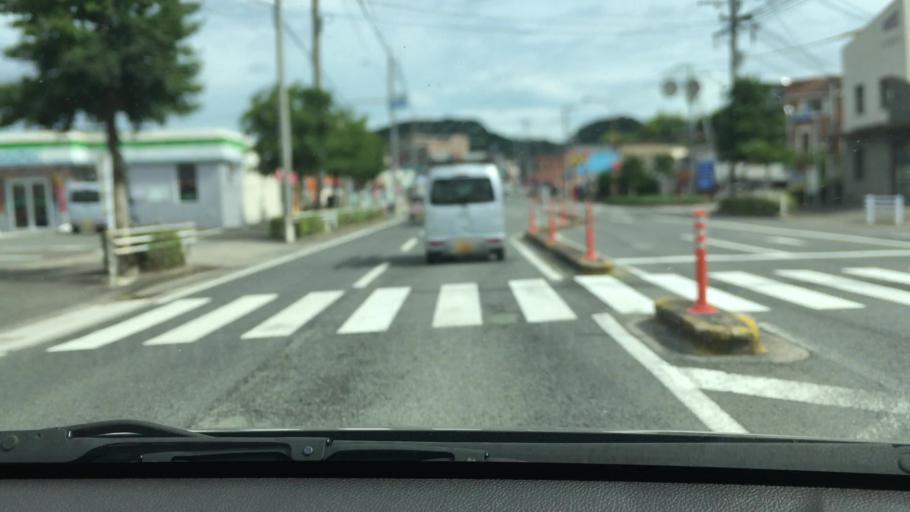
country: JP
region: Nagasaki
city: Togitsu
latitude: 32.8417
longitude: 129.8369
